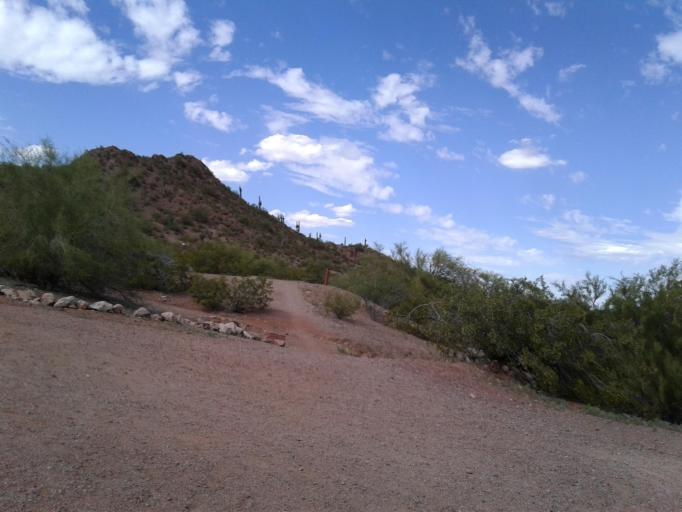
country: US
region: Arizona
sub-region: Maricopa County
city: Tempe Junction
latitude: 33.4559
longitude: -111.9440
